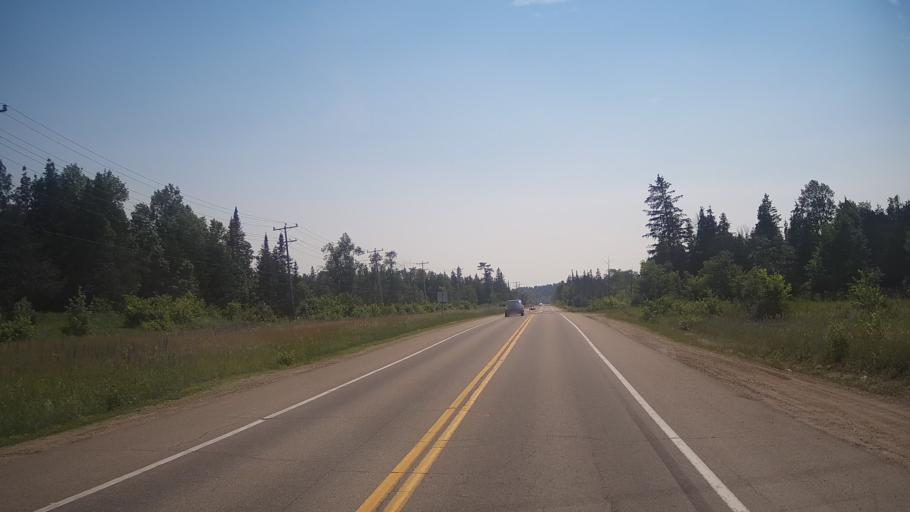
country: CA
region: Ontario
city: Pembroke
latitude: 45.8235
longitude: -77.0190
